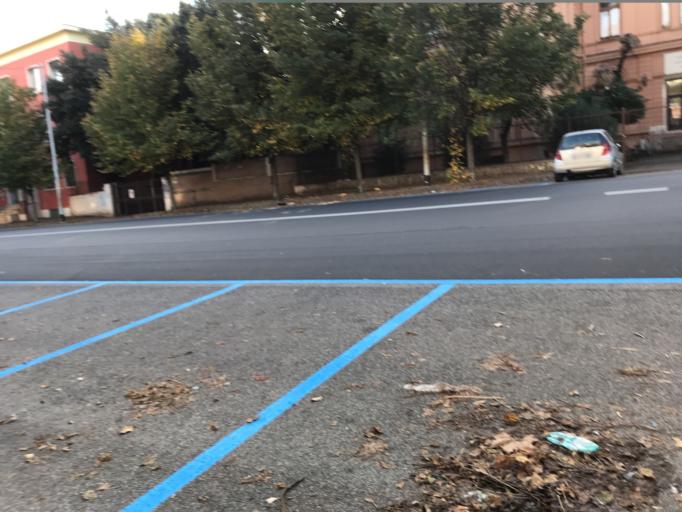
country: IT
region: Latium
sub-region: Citta metropolitana di Roma Capitale
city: Rome
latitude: 41.9049
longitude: 12.5132
